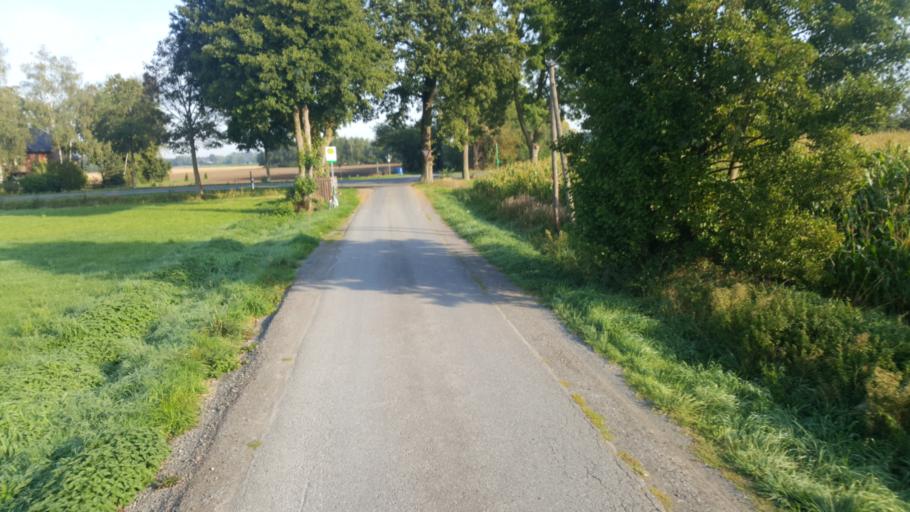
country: DE
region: North Rhine-Westphalia
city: Rietberg
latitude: 51.7403
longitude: 8.4139
